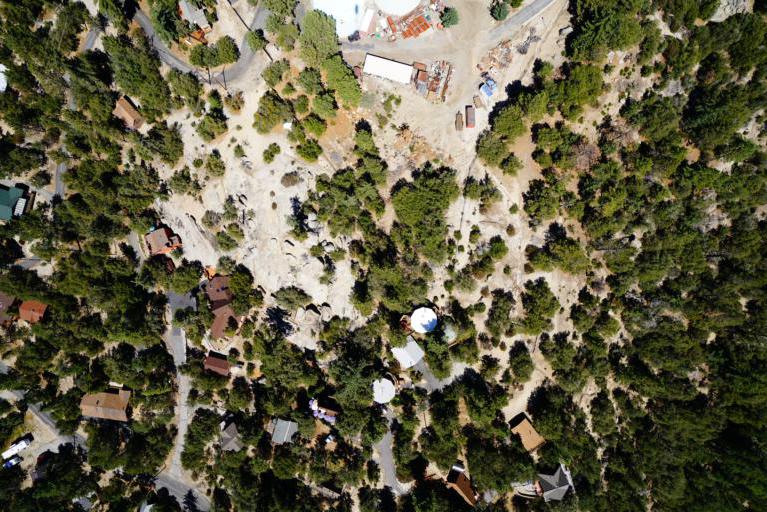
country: US
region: California
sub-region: Riverside County
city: Idyllwild-Pine Cove
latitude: 33.7644
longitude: -116.7333
